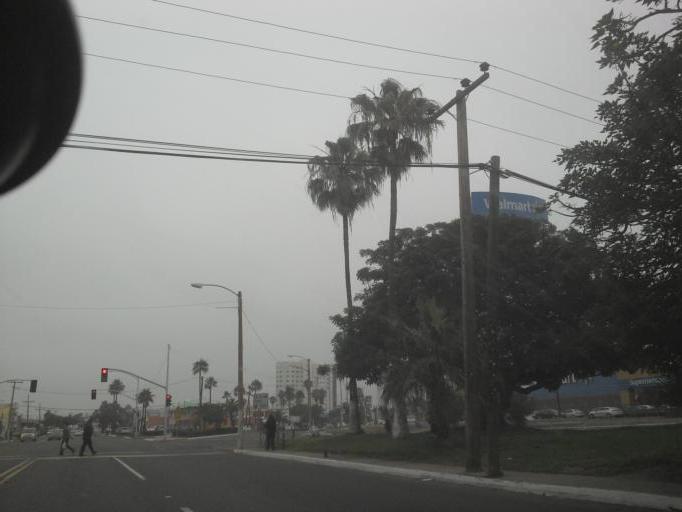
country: US
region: California
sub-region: San Diego County
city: Imperial Beach
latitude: 32.5275
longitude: -117.1200
